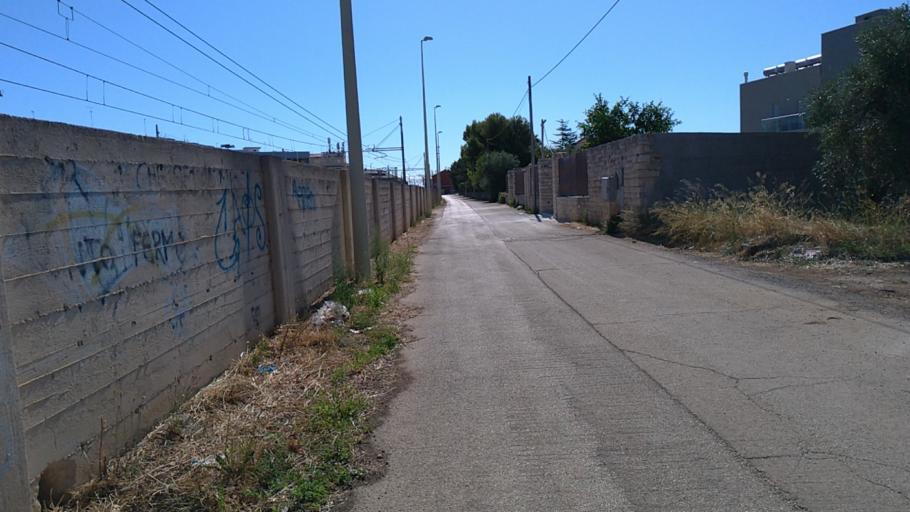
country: IT
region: Apulia
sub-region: Provincia di Bari
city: Giovinazzo
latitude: 41.1808
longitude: 16.6696
